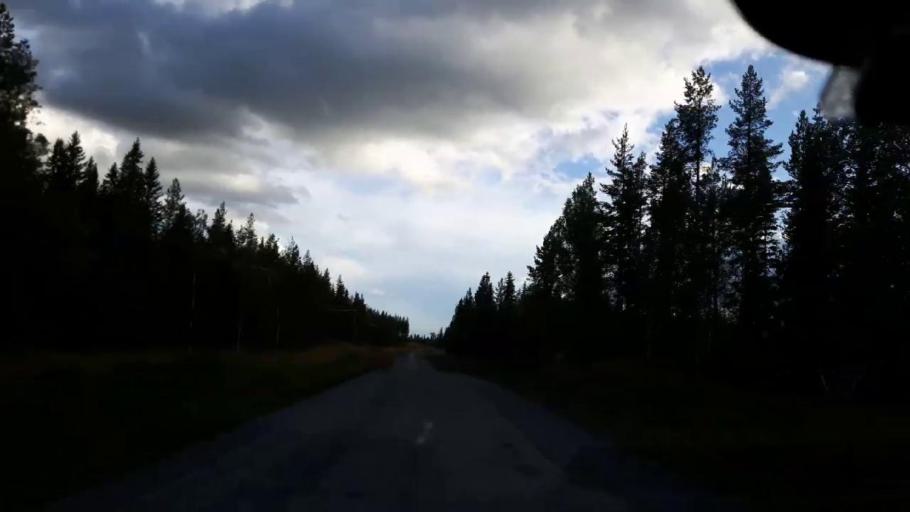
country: SE
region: Jaemtland
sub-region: Stroemsunds Kommun
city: Stroemsund
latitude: 63.3259
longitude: 15.5807
